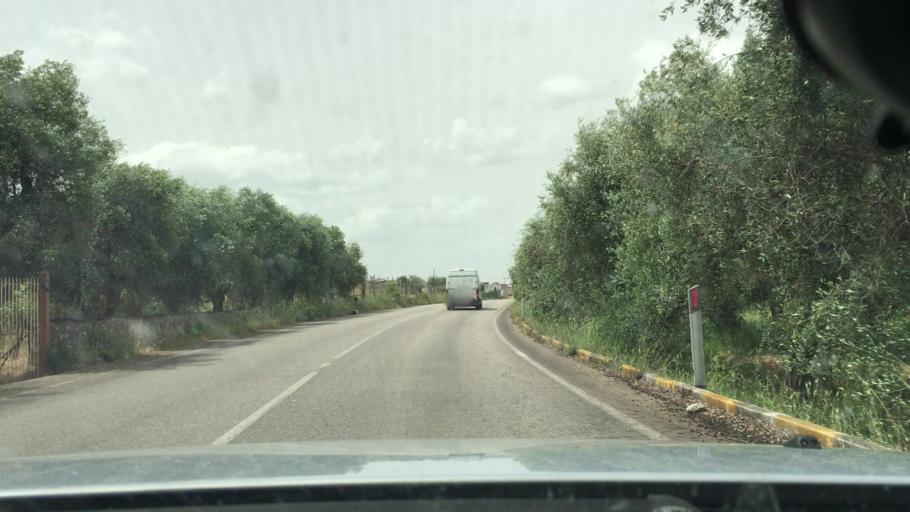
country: IT
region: Apulia
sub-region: Provincia di Bari
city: Capurso
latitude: 41.0425
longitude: 16.9406
